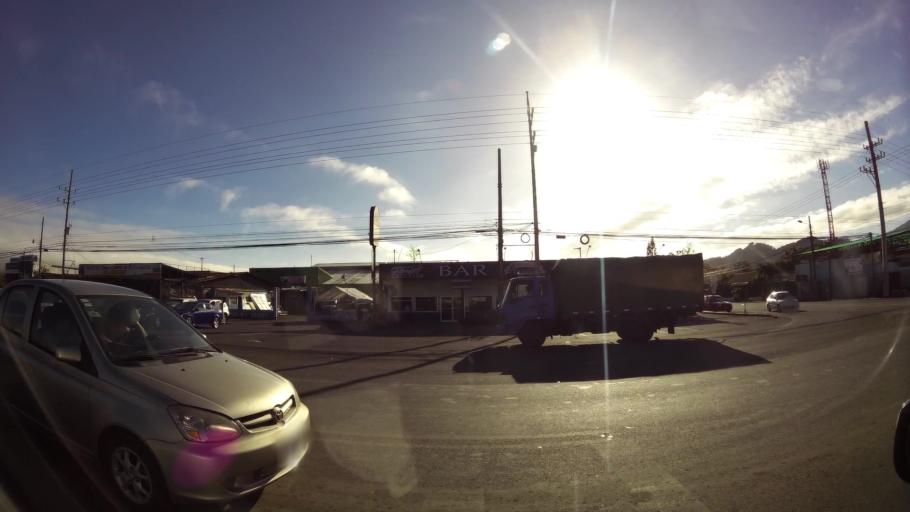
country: CR
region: Cartago
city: Tobosi
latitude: 9.8428
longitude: -83.9505
